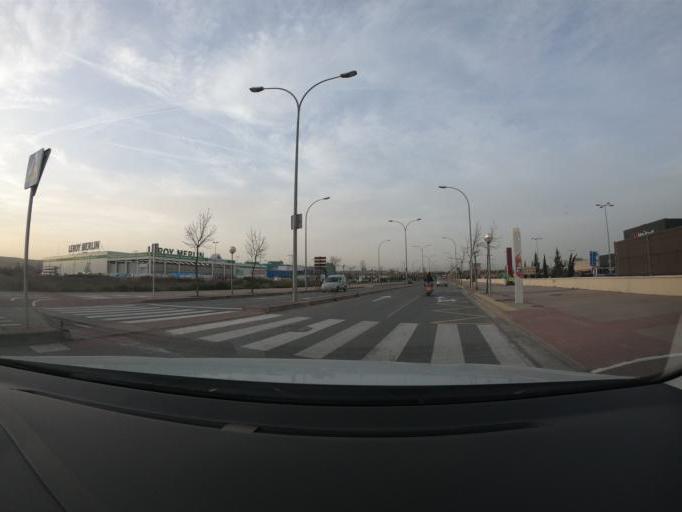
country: ES
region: La Rioja
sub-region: Provincia de La Rioja
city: Lardero
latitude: 42.4509
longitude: -2.4711
